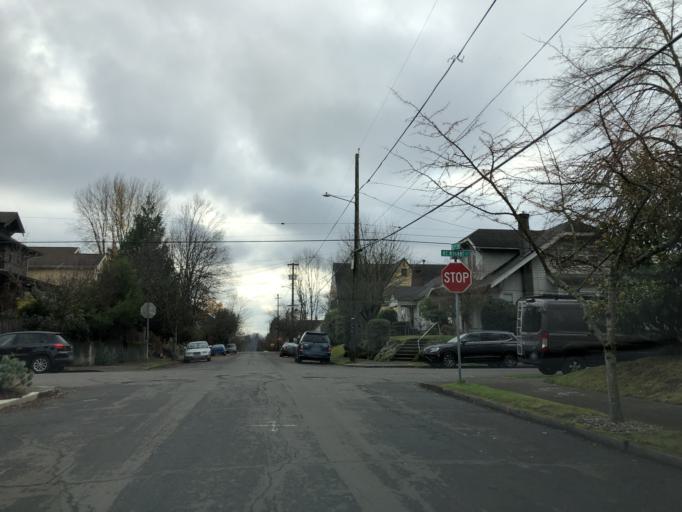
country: US
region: Washington
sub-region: Clark County
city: Vancouver
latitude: 45.6018
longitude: -122.6310
